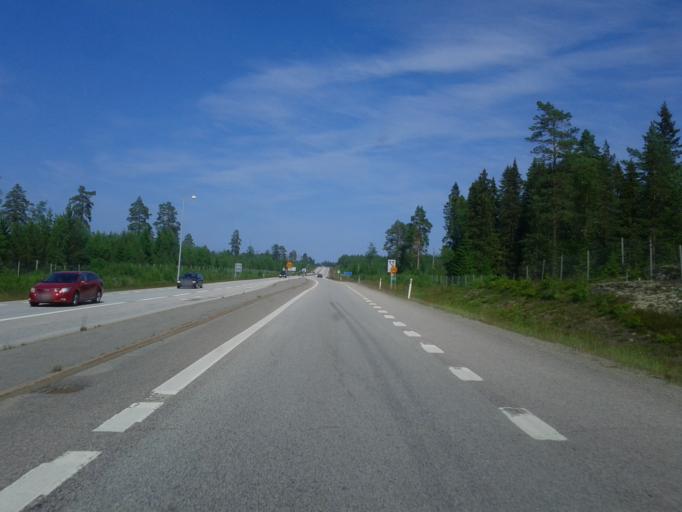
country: SE
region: Vaesterbotten
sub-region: Umea Kommun
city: Hoernefors
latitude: 63.6413
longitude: 19.9240
